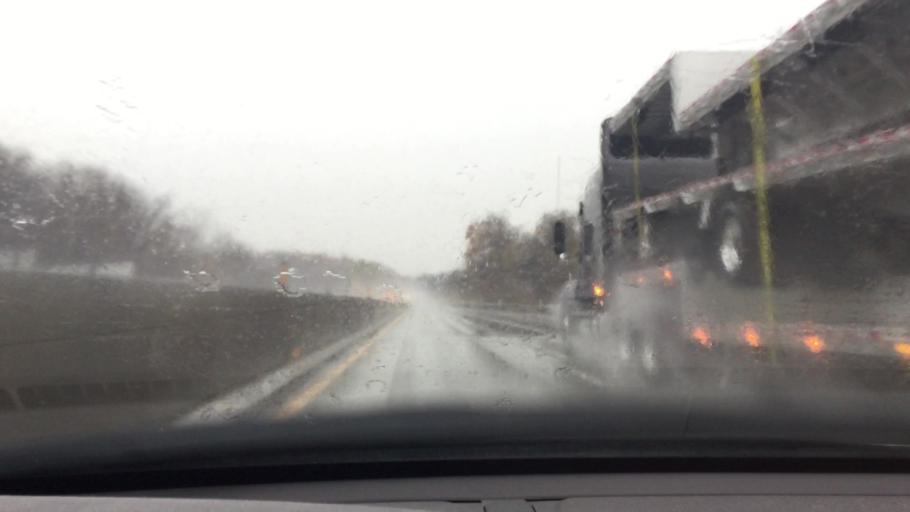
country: US
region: Pennsylvania
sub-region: Washington County
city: Ellsworth
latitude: 40.1671
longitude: -80.0870
